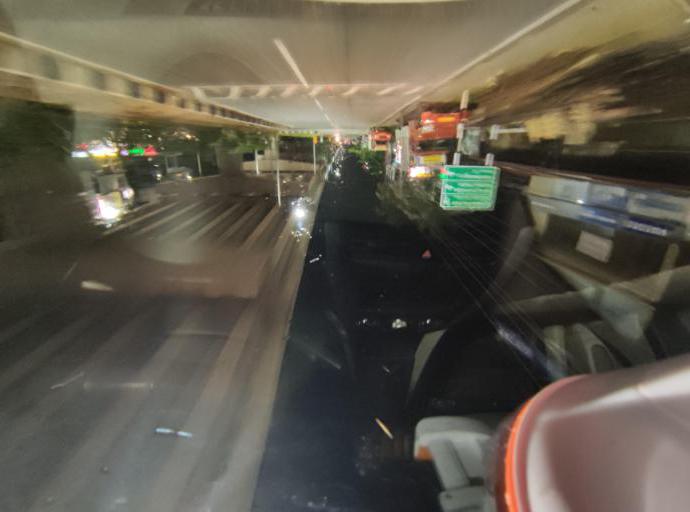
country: IN
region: Kerala
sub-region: Thiruvananthapuram
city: Thiruvananthapuram
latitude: 8.4867
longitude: 76.9279
